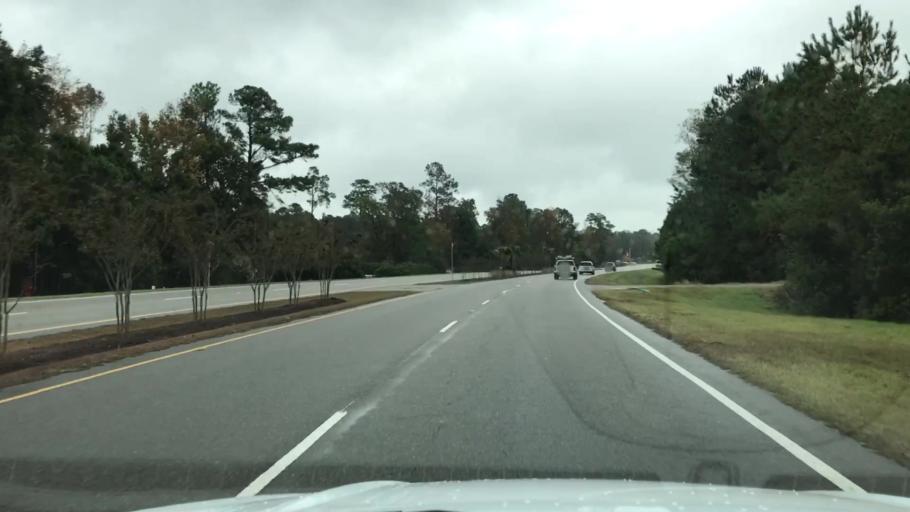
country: US
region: South Carolina
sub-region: Horry County
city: Myrtle Beach
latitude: 33.7578
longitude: -78.8642
